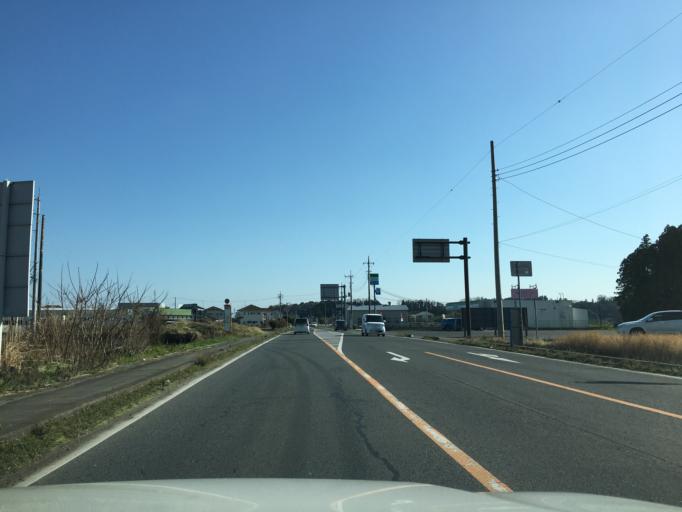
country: JP
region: Ibaraki
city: Omiya
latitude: 36.4507
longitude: 140.4087
